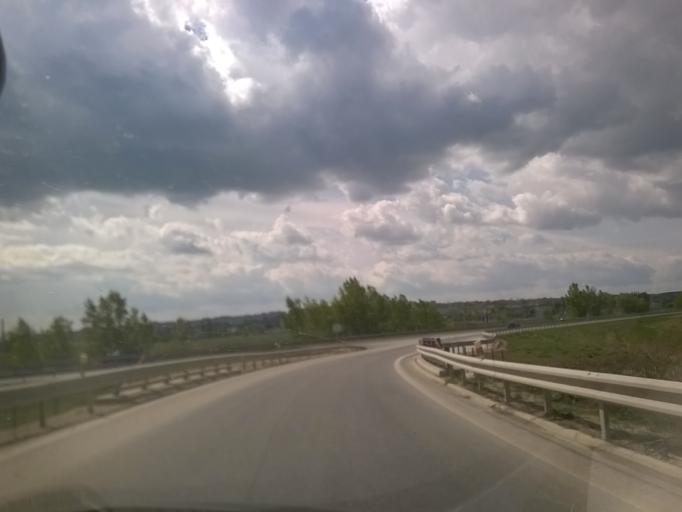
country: SK
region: Nitriansky
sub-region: Okres Nitra
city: Nitra
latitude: 48.3260
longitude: 18.0615
